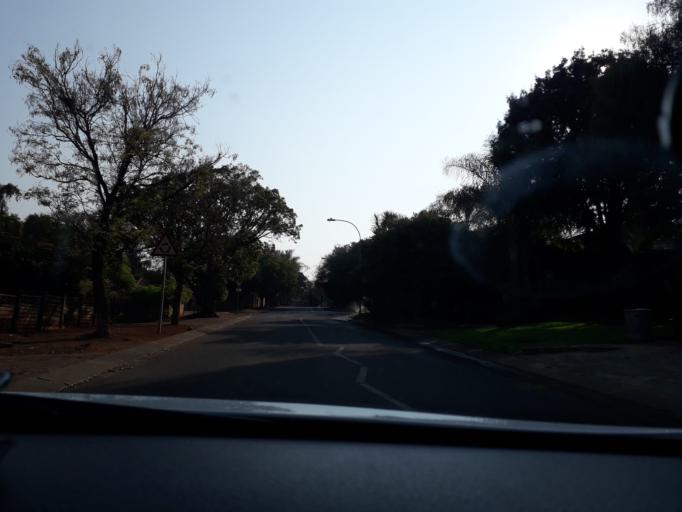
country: ZA
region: Gauteng
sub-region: City of Tshwane Metropolitan Municipality
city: Centurion
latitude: -25.8961
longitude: 28.1487
